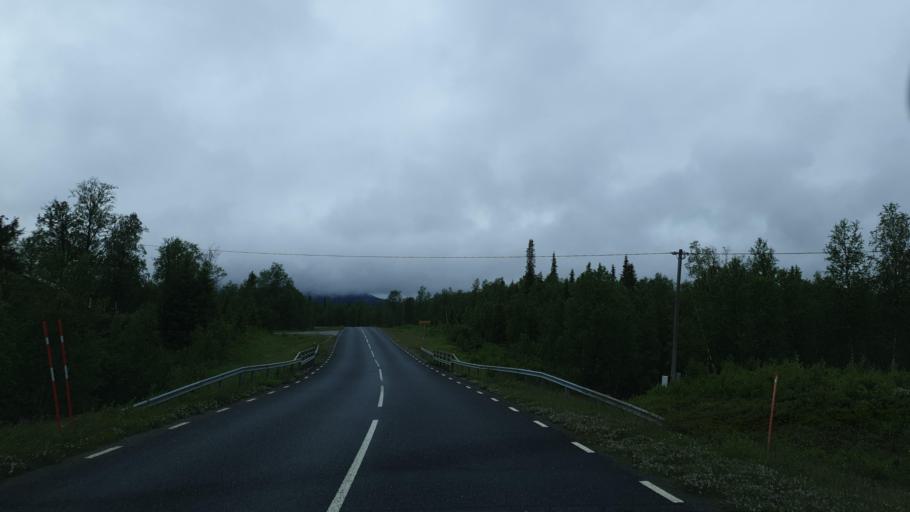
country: SE
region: Vaesterbotten
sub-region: Vilhelmina Kommun
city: Sjoberg
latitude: 65.2563
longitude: 15.7196
